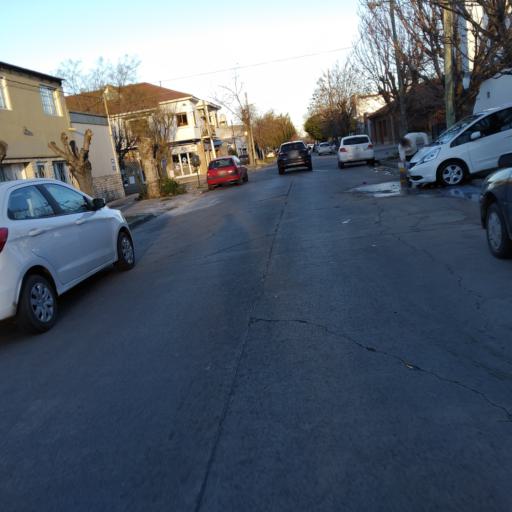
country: AR
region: Buenos Aires
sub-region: Partido de La Plata
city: La Plata
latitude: -34.9438
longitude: -57.9611
